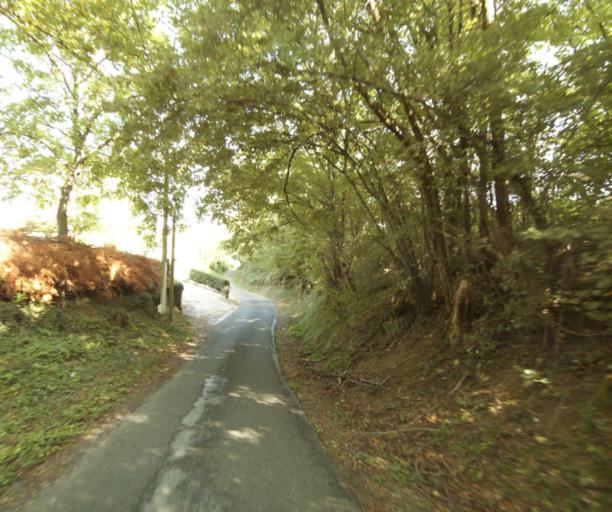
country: FR
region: Bourgogne
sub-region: Departement de Saone-et-Loire
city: Tournus
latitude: 46.5610
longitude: 4.8800
